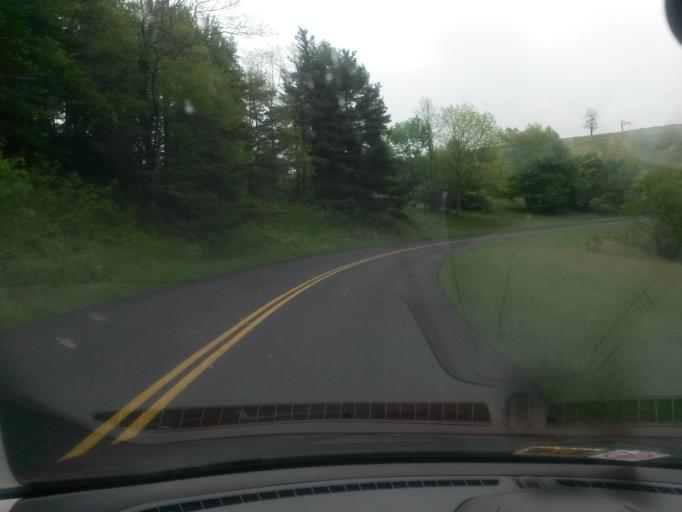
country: US
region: Virginia
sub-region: Floyd County
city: Floyd
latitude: 36.8280
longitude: -80.3448
